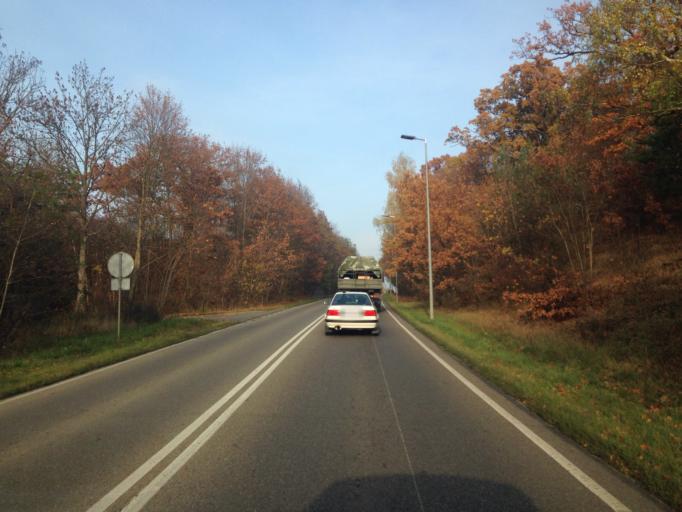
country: PL
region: Kujawsko-Pomorskie
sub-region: Powiat bydgoski
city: Osielsko
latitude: 53.1676
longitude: 18.0462
